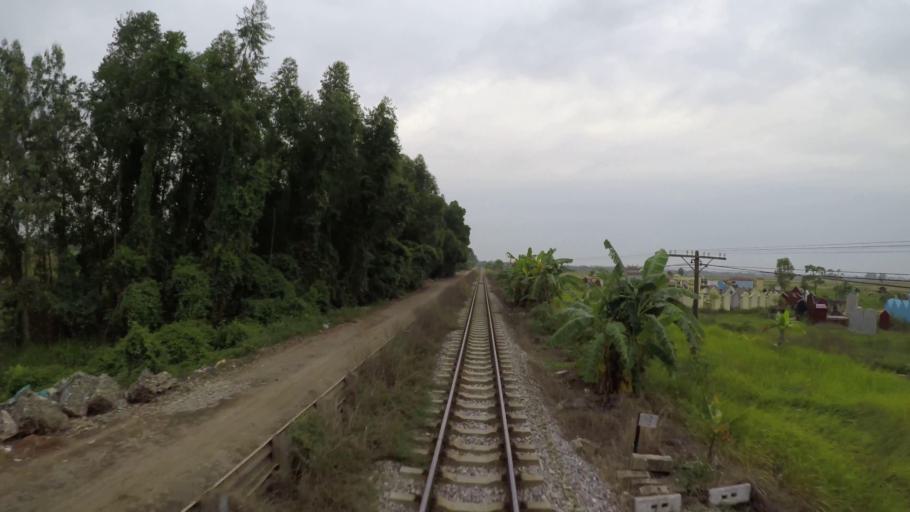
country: VN
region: Hai Duong
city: Ke Sat
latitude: 20.9658
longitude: 106.1320
